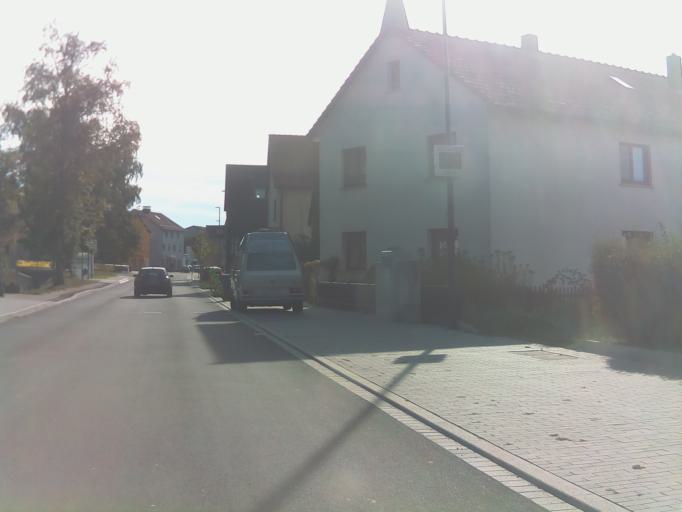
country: DE
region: Hesse
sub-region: Regierungsbezirk Kassel
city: Dipperz
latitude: 50.5442
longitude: 9.7983
